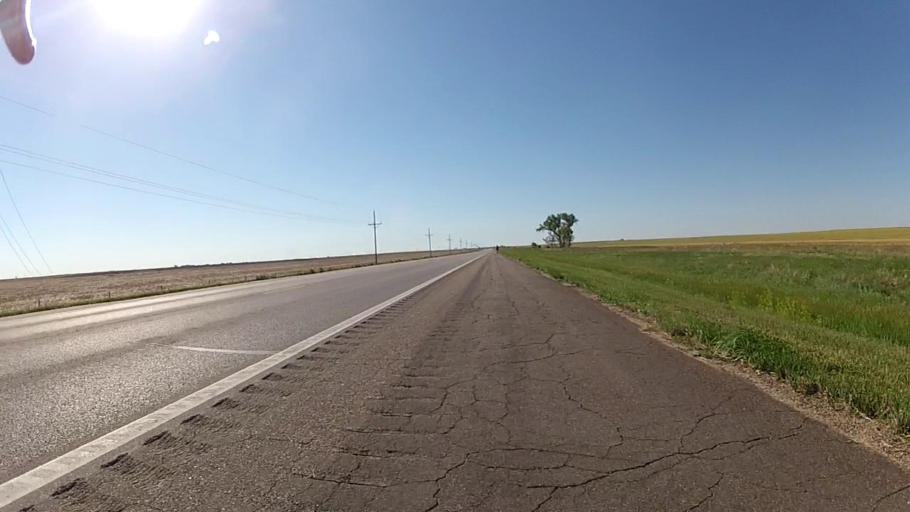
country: US
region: Kansas
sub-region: Ford County
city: Dodge City
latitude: 37.5931
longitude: -99.6919
